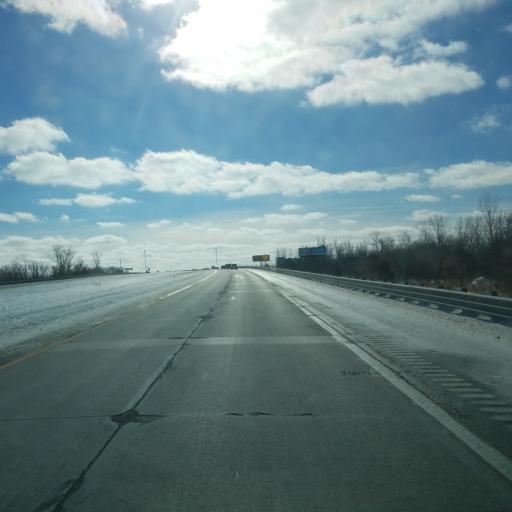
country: US
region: Michigan
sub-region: Ingham County
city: East Lansing
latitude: 42.7751
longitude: -84.5141
